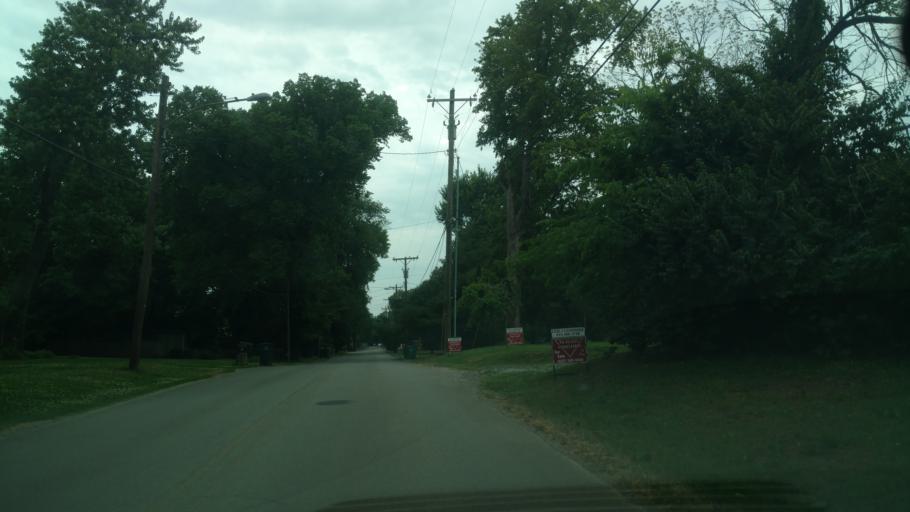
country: US
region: Tennessee
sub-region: Davidson County
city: Nashville
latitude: 36.1890
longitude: -86.7237
